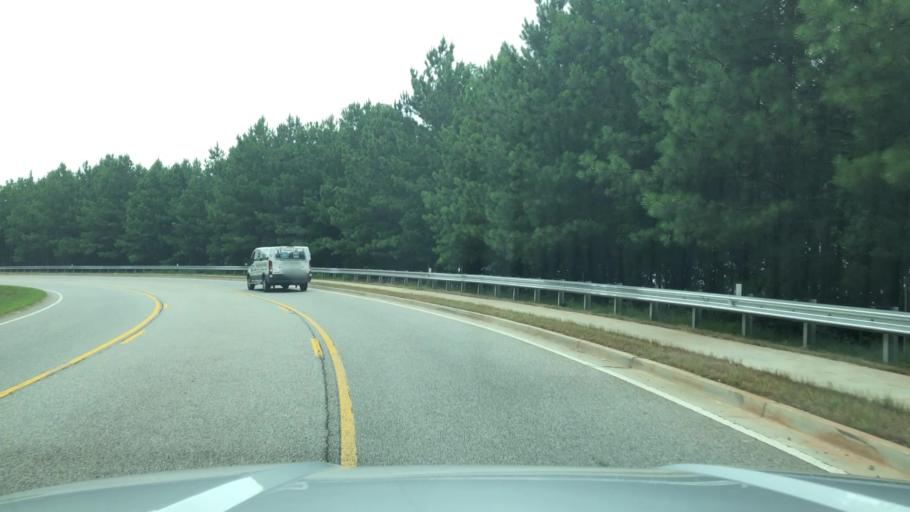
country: US
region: Georgia
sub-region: Cobb County
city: Mableton
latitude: 33.7735
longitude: -84.5809
